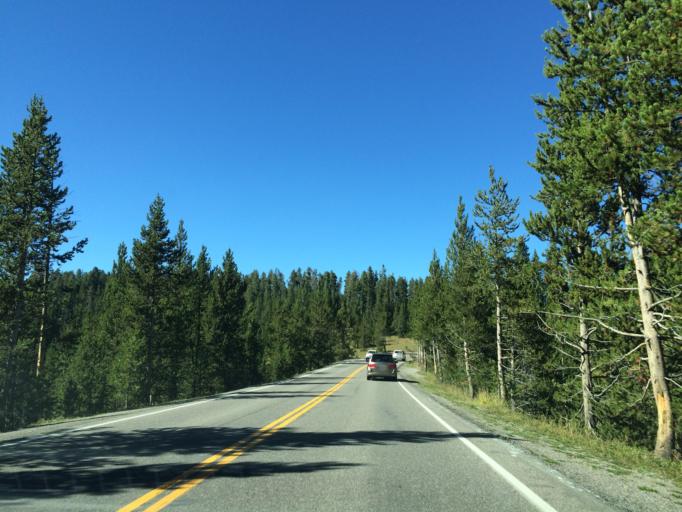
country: US
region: Montana
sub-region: Gallatin County
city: West Yellowstone
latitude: 44.7142
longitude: -110.5044
